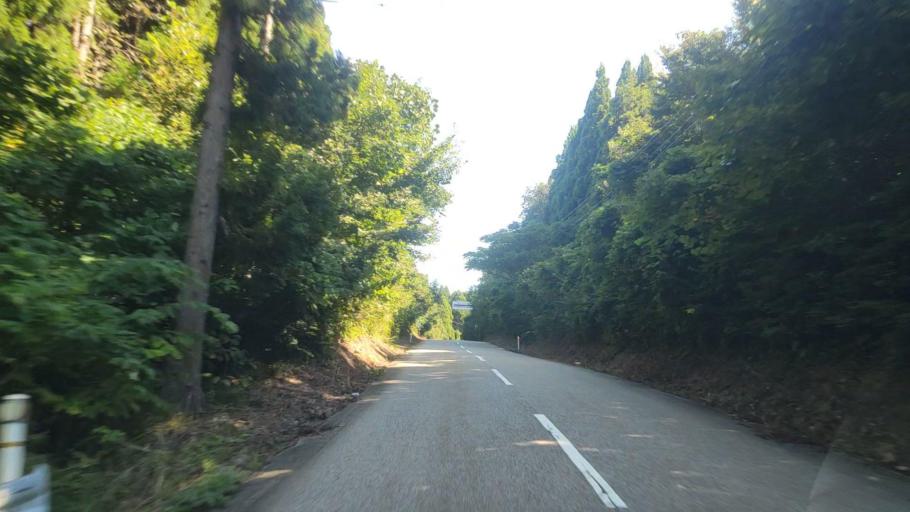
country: JP
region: Ishikawa
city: Nanao
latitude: 37.5142
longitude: 137.3339
